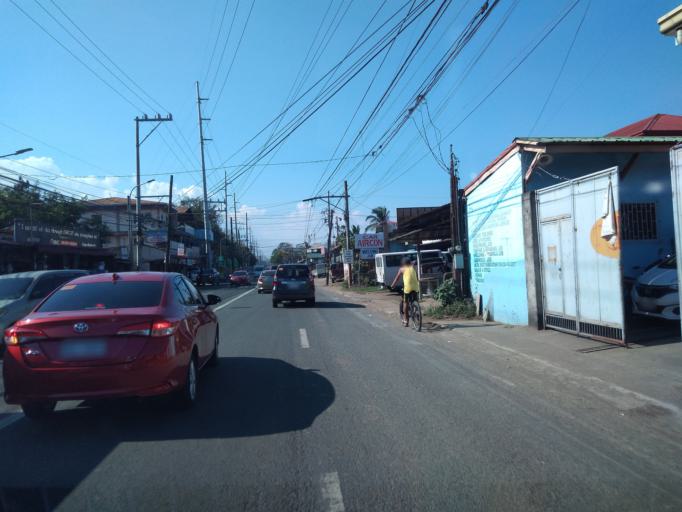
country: PH
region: Calabarzon
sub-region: Province of Laguna
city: Calamba
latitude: 14.1882
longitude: 121.1701
